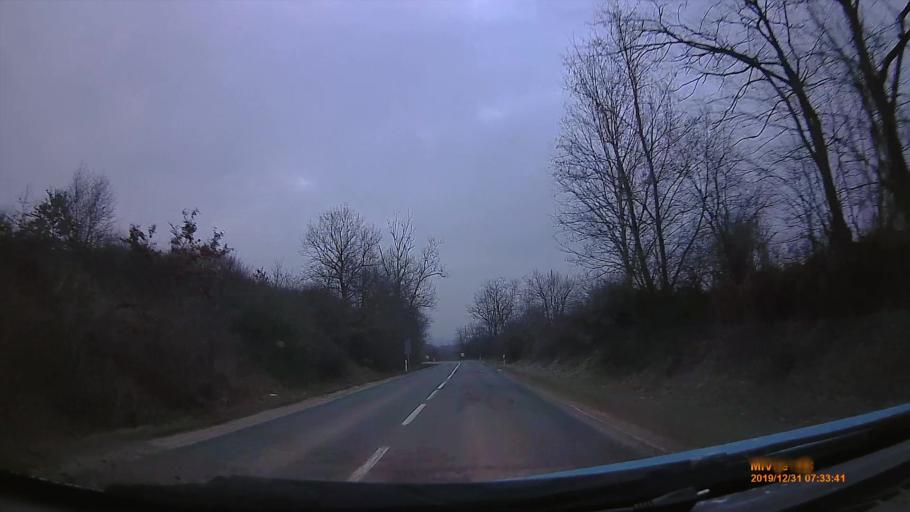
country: HU
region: Heves
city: Recsk
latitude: 47.9252
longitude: 20.1379
